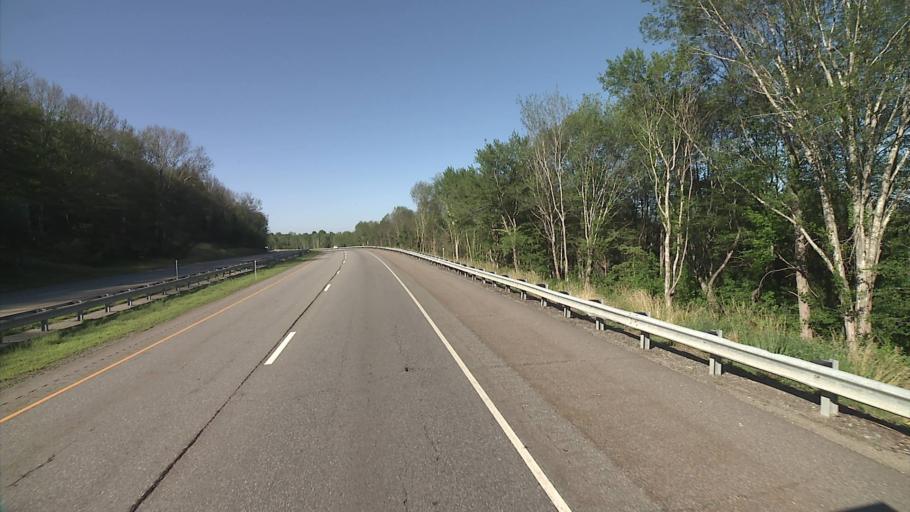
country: US
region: Connecticut
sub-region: Windham County
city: Plainfield Village
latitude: 41.6481
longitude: -71.9328
